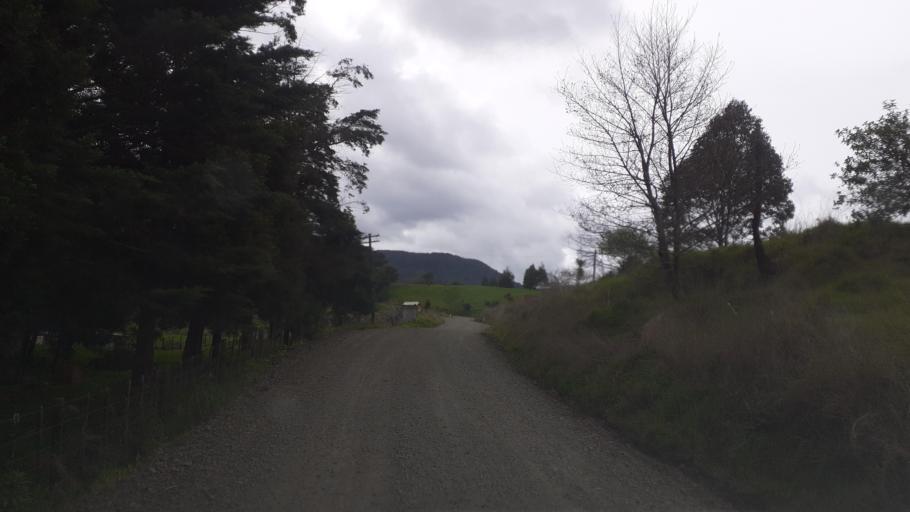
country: NZ
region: Northland
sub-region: Far North District
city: Waimate North
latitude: -35.5680
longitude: 173.5292
